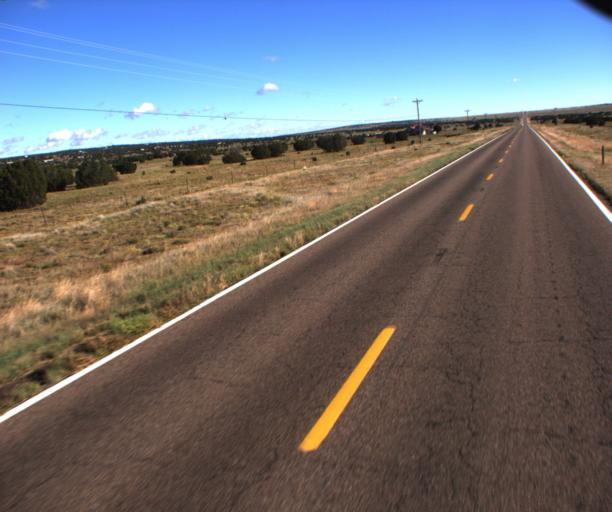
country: US
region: Arizona
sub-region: Navajo County
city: White Mountain Lake
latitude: 34.3402
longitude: -109.7336
